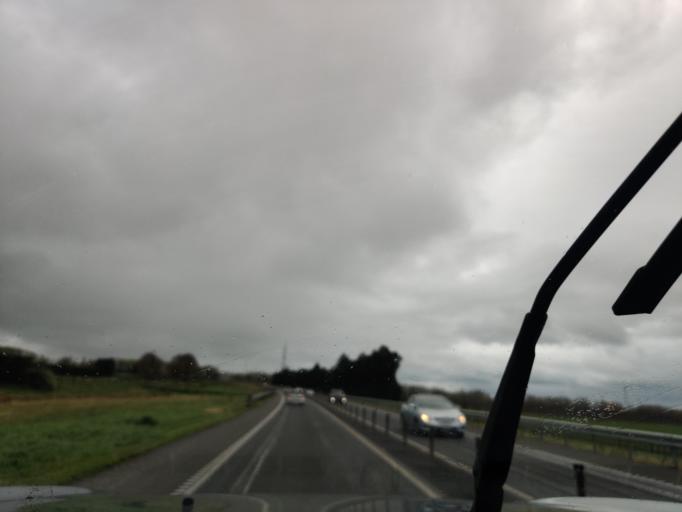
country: NZ
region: Hawke's Bay
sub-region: Hastings District
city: Hastings
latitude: -39.6013
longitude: 176.8445
